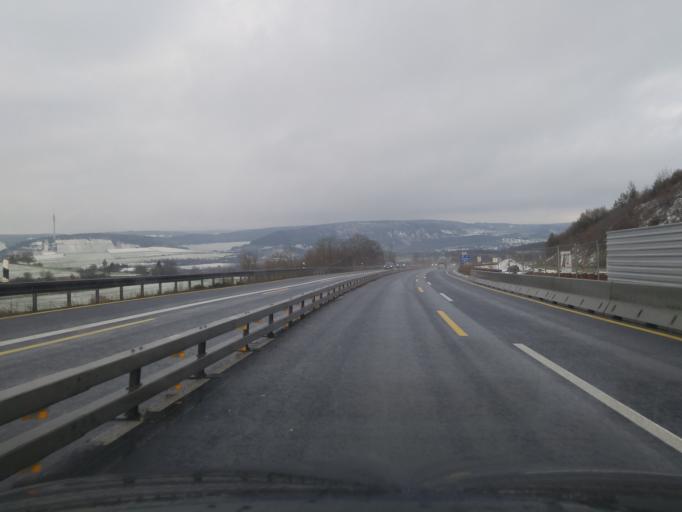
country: DE
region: Bavaria
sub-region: Regierungsbezirk Unterfranken
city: Fuchsstadt
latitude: 50.1127
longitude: 9.9577
